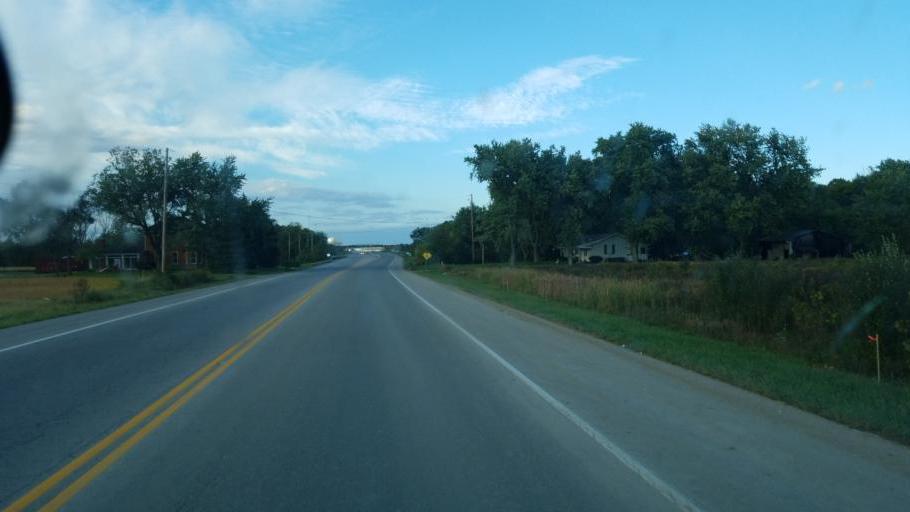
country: US
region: Ohio
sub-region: Franklin County
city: New Albany
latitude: 40.0723
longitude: -82.7540
